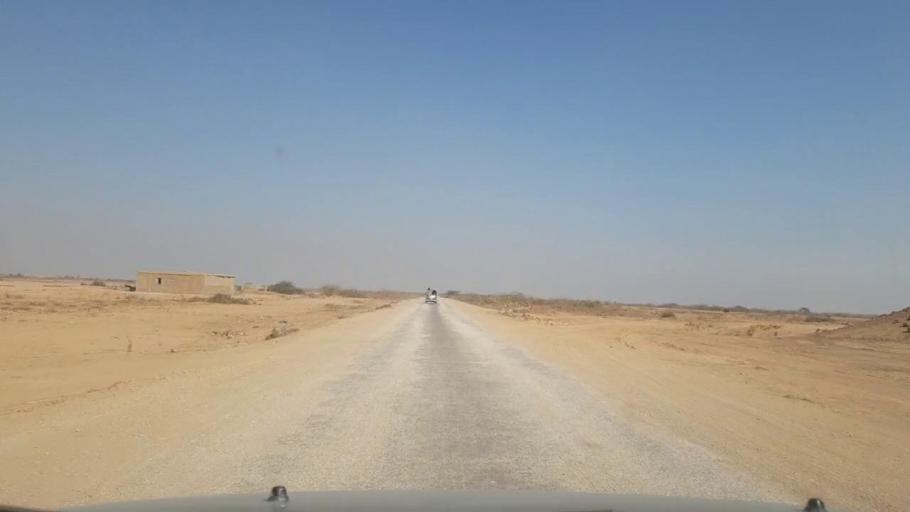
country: PK
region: Sindh
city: Thatta
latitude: 24.8901
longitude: 67.9133
